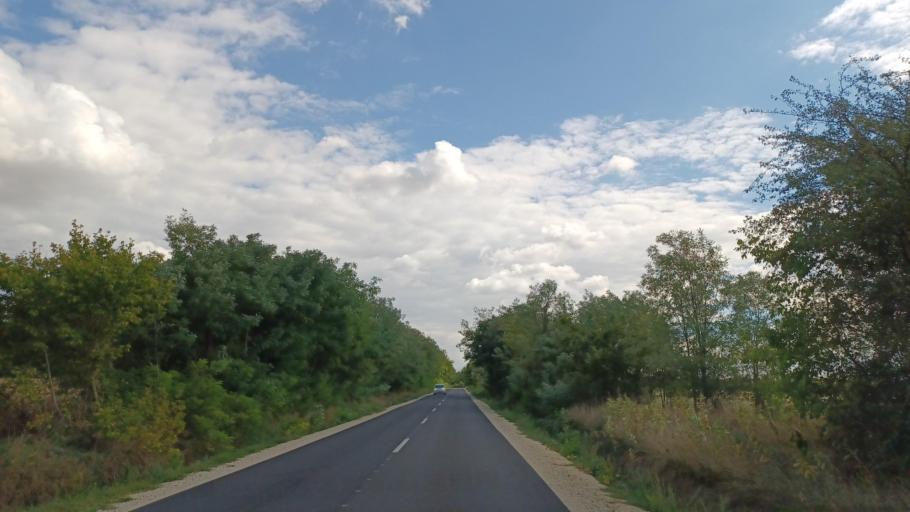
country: HU
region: Tolna
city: Nagydorog
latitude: 46.6035
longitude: 18.6962
